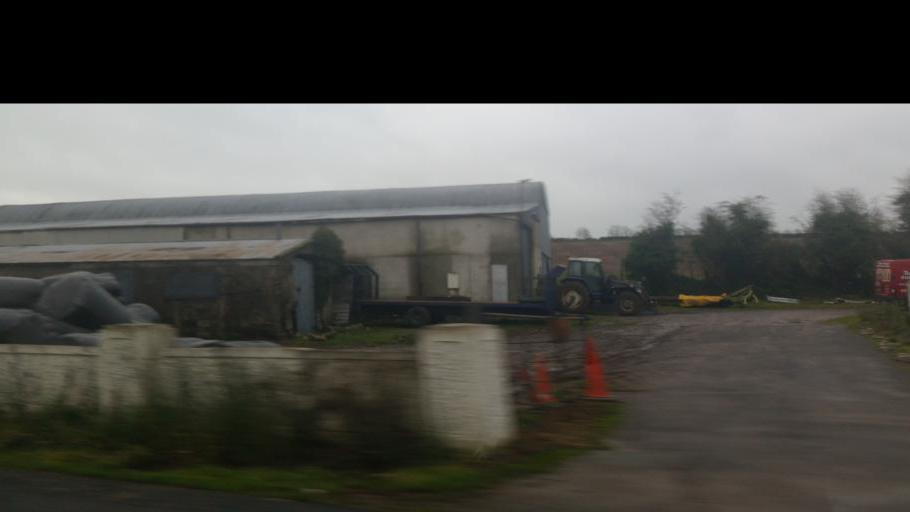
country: IE
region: Leinster
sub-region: Kildare
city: Castledermot
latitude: 52.8950
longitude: -6.8536
